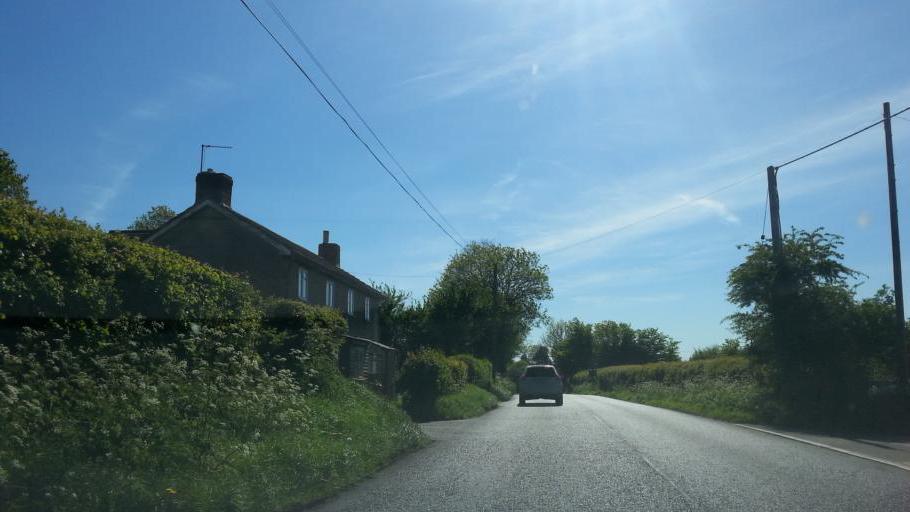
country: GB
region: England
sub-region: Dorset
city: Gillingham
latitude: 51.0107
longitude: -2.2542
